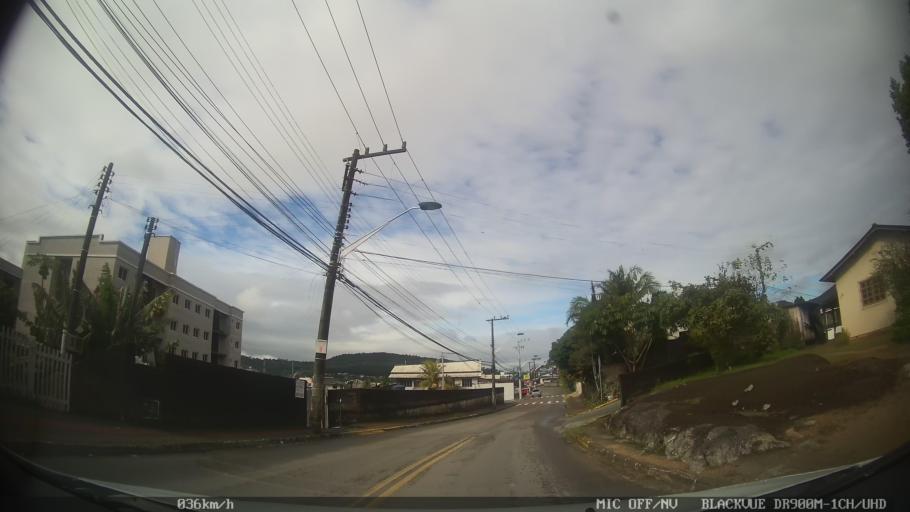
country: BR
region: Santa Catarina
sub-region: Biguacu
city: Biguacu
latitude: -27.5093
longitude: -48.6571
